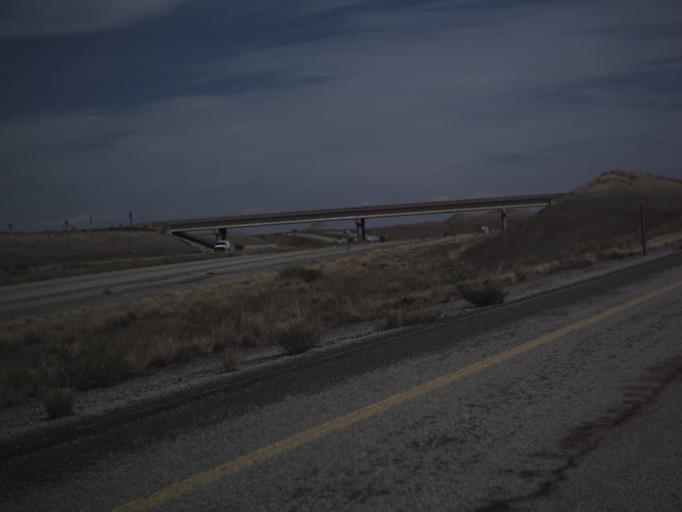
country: US
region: Utah
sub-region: Grand County
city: Moab
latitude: 38.9366
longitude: -109.4103
